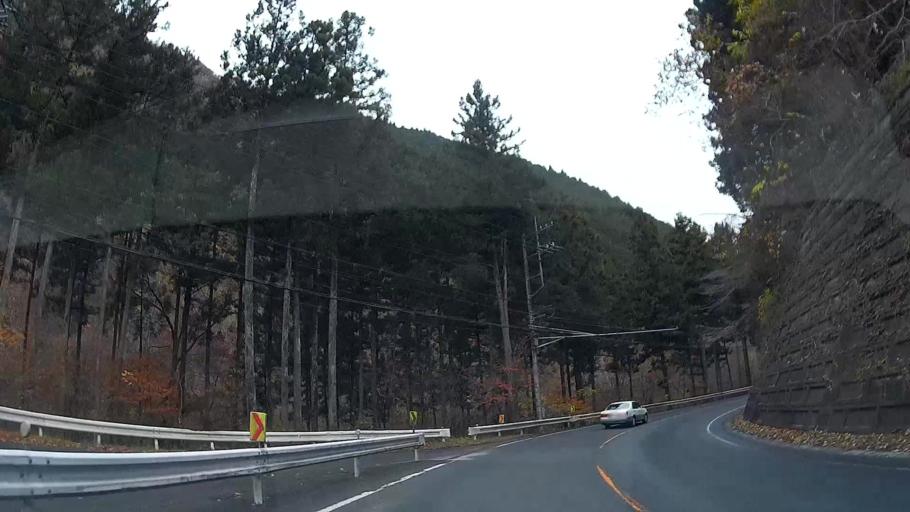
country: JP
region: Saitama
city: Chichibu
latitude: 35.9368
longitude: 138.9610
